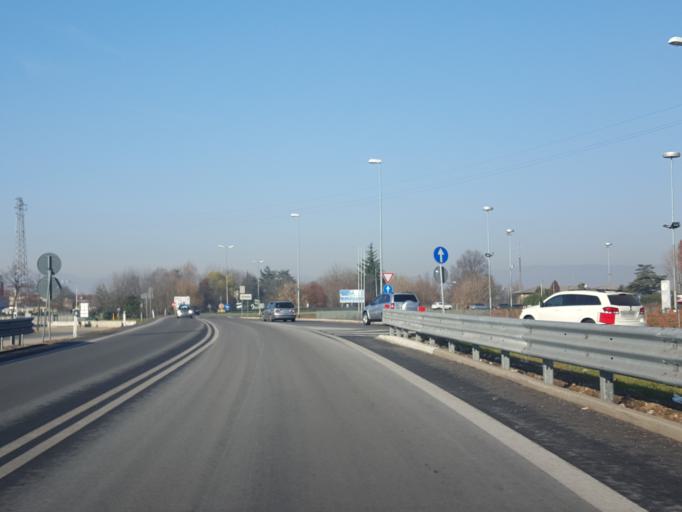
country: IT
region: Veneto
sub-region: Provincia di Vicenza
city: Villaggio Montegrappa
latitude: 45.5294
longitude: 11.5926
